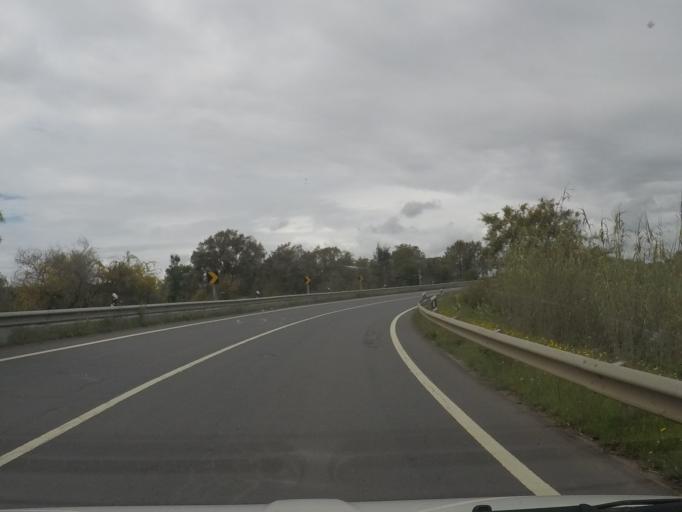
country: PT
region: Setubal
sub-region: Santiago do Cacem
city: Cercal
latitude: 37.8369
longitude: -8.7045
